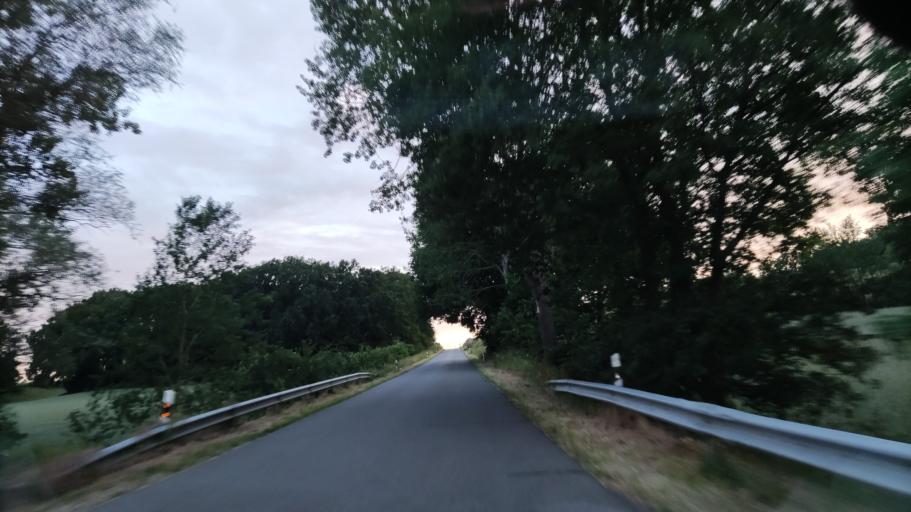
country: DE
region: Lower Saxony
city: Neu Darchau
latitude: 53.1999
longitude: 10.9490
